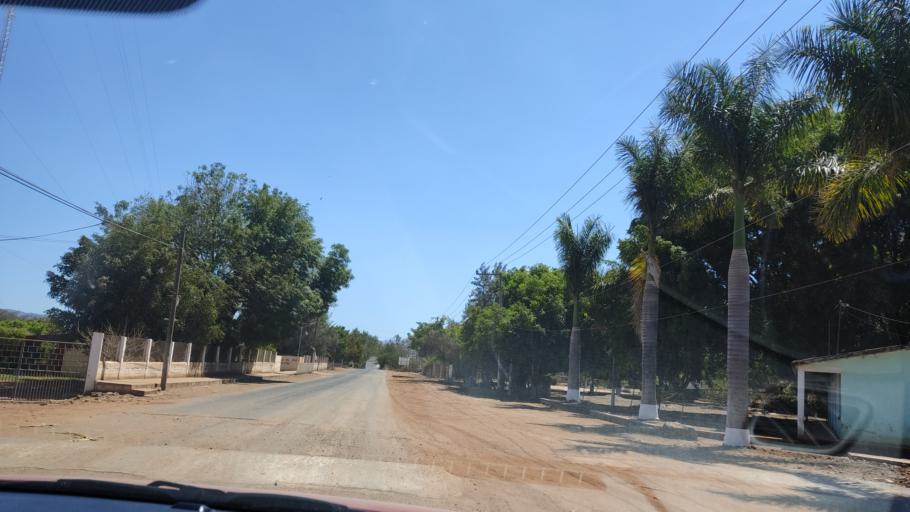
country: MX
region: Nayarit
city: Santa Maria del Oro
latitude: 21.4219
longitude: -104.6104
